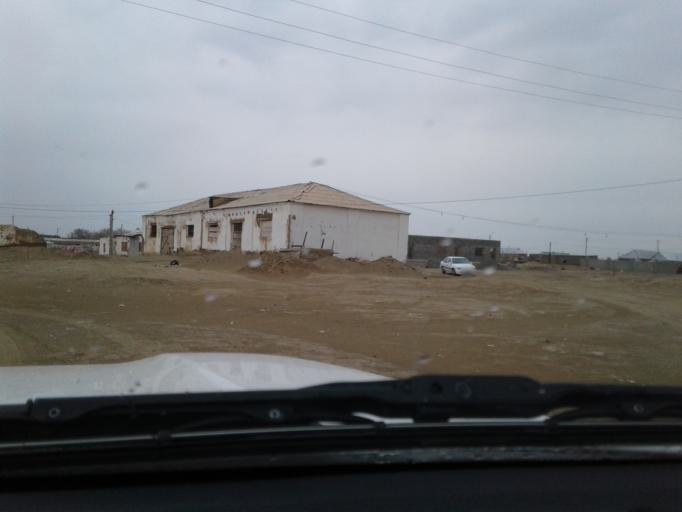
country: TM
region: Ahal
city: Abadan
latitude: 38.7614
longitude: 58.4927
